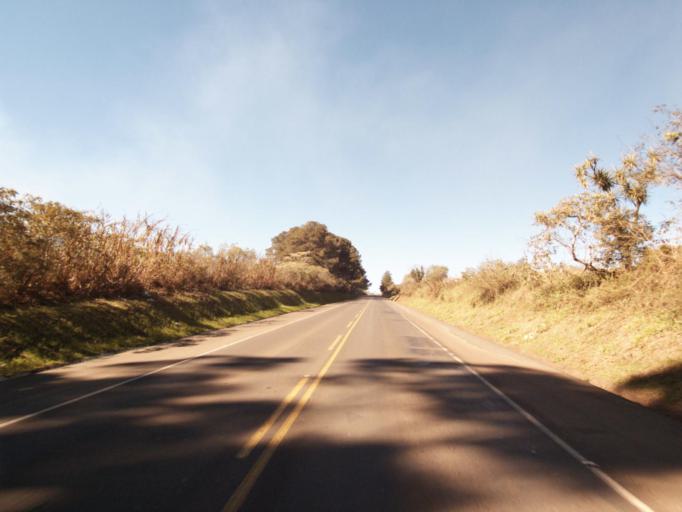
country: BR
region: Santa Catarina
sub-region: Chapeco
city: Chapeco
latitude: -27.0005
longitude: -52.6566
